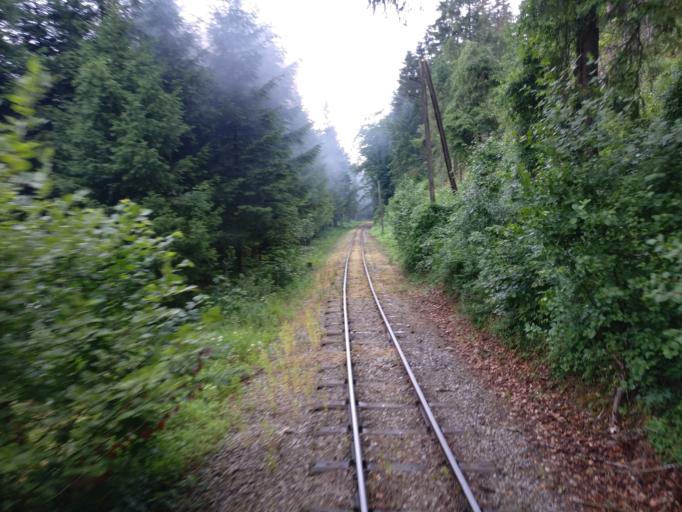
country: AT
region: Upper Austria
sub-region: Politischer Bezirk Steyr-Land
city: Waldneukirchen
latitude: 47.9987
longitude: 14.2835
